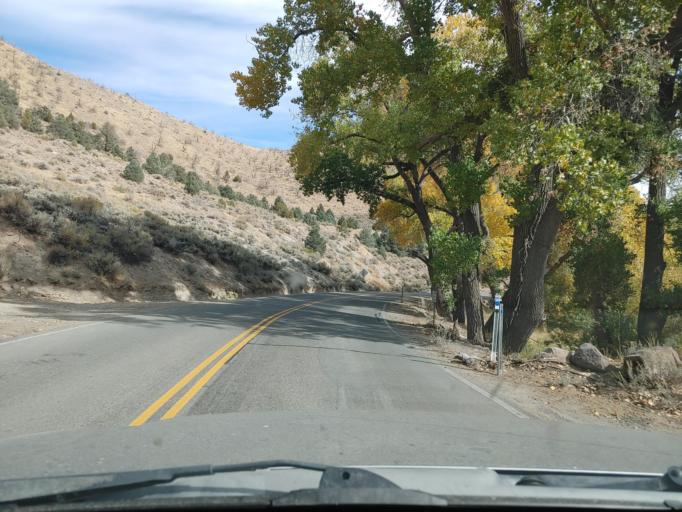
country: US
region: Nevada
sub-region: Storey County
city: Virginia City
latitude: 39.3062
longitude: -119.6147
